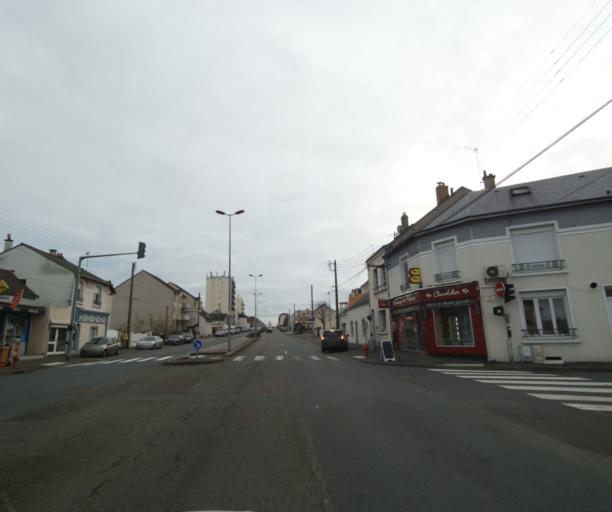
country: FR
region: Pays de la Loire
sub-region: Departement de la Sarthe
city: Le Mans
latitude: 47.9745
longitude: 0.2065
